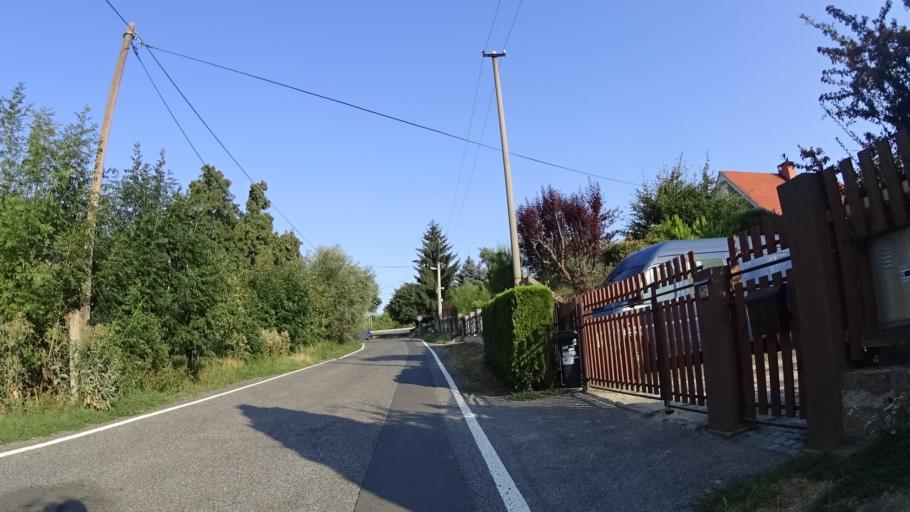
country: CZ
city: Ohrazenice
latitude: 50.6198
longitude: 15.1113
